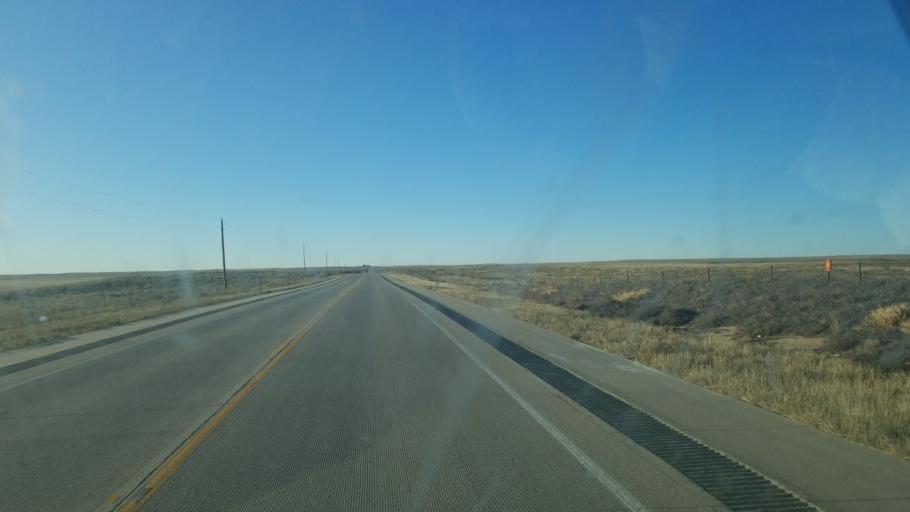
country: US
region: Colorado
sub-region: Kiowa County
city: Eads
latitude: 38.6291
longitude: -102.7860
